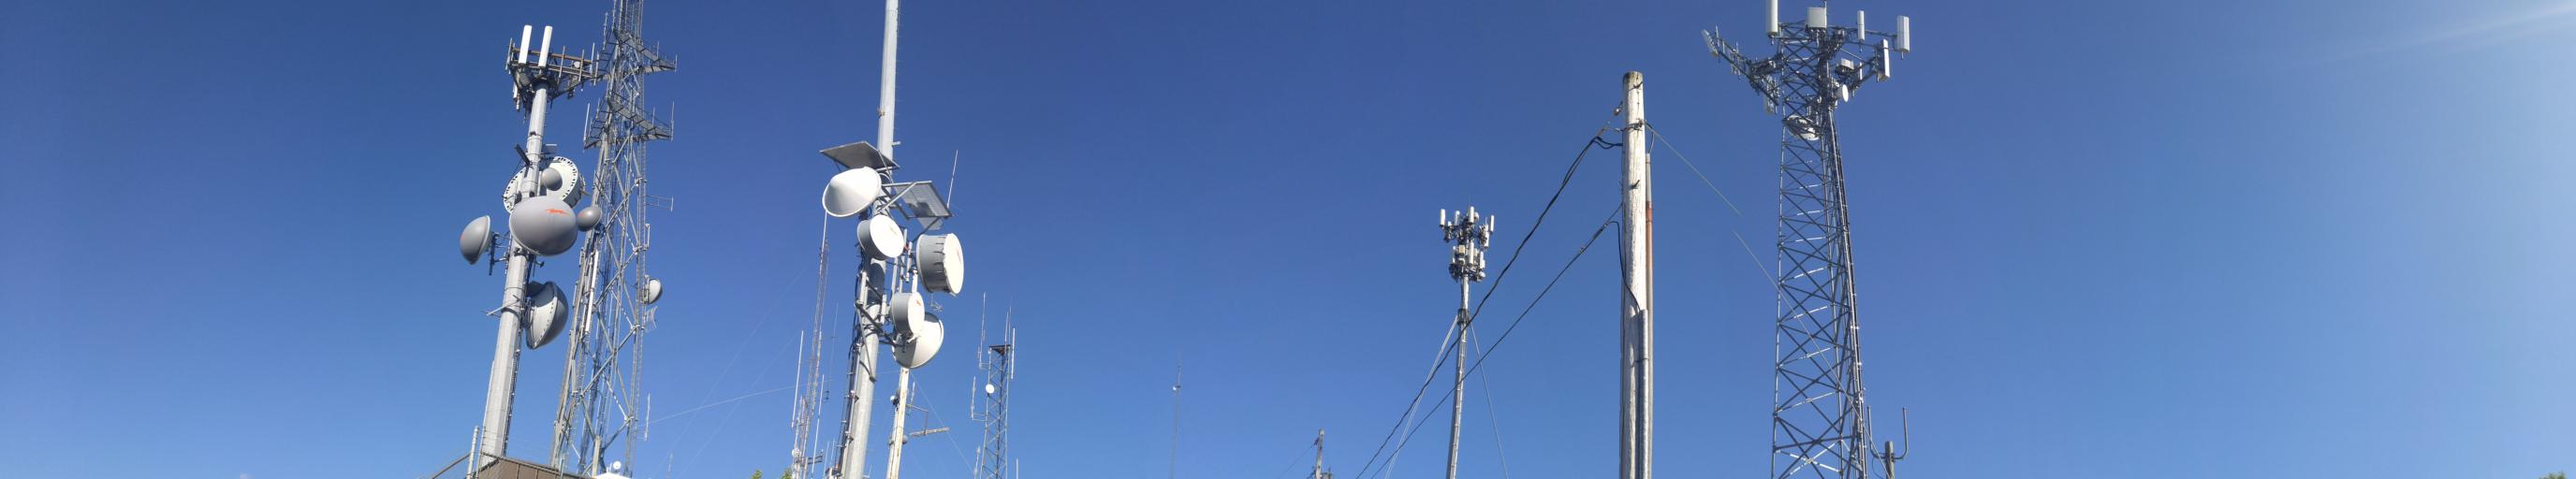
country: US
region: North Carolina
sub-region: Haywood County
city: Clyde
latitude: 35.5686
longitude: -82.9079
